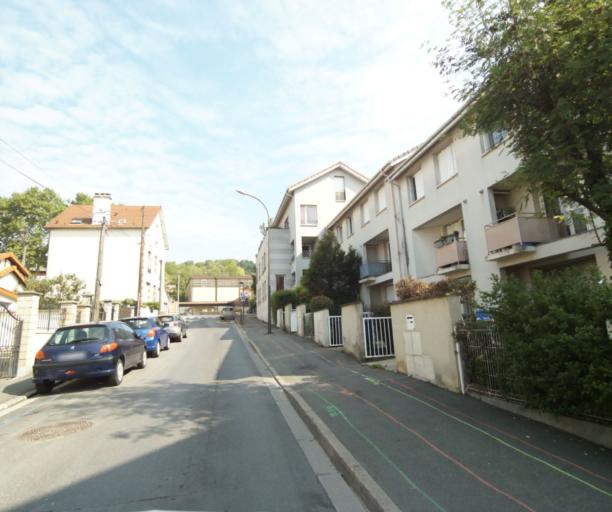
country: FR
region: Ile-de-France
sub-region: Departement du Val-d'Oise
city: Sannois
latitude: 48.9602
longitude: 2.2516
